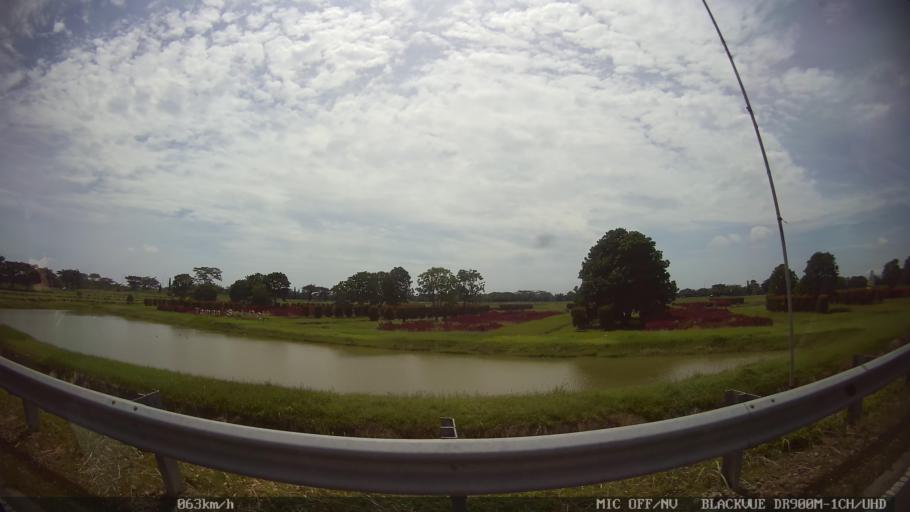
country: ID
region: North Sumatra
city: Percut
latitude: 3.6315
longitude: 98.8731
